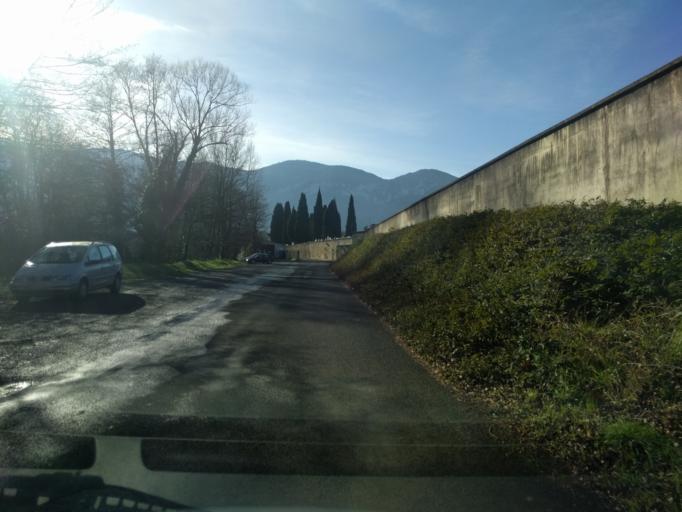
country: FR
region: Languedoc-Roussillon
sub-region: Departement de l'Aude
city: Quillan
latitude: 42.8801
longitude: 2.1876
